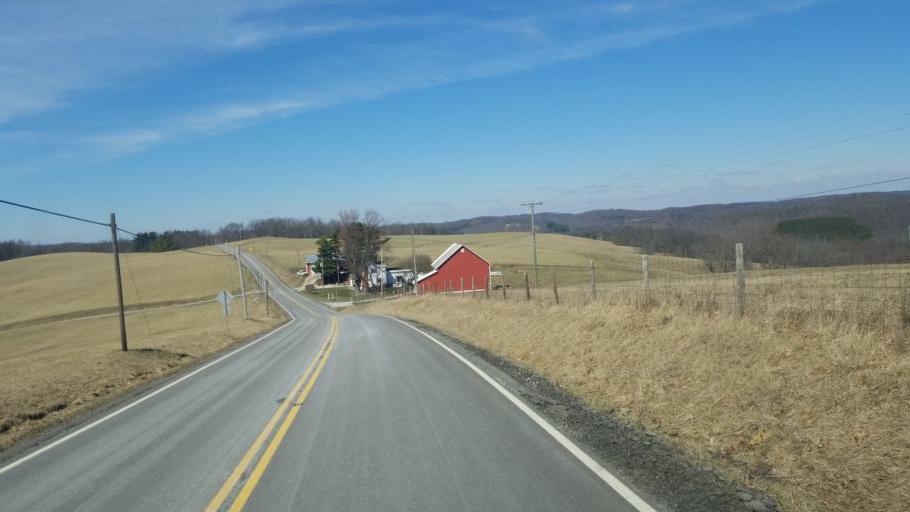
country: US
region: Ohio
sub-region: Knox County
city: Danville
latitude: 40.4940
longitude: -82.2203
